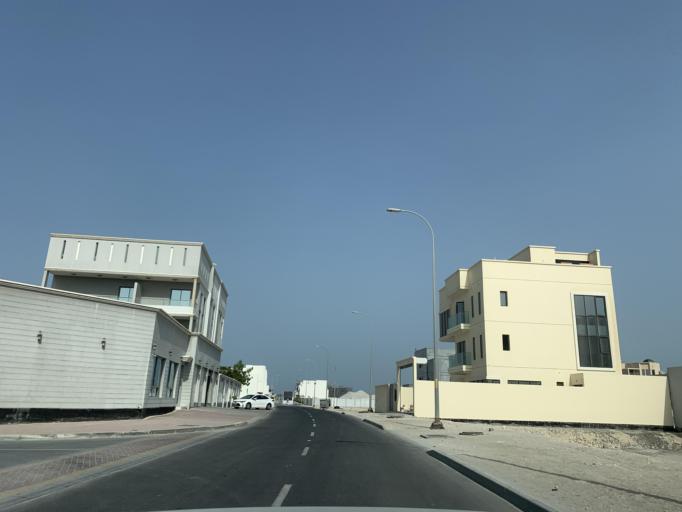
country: BH
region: Muharraq
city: Al Muharraq
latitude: 26.3104
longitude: 50.6340
